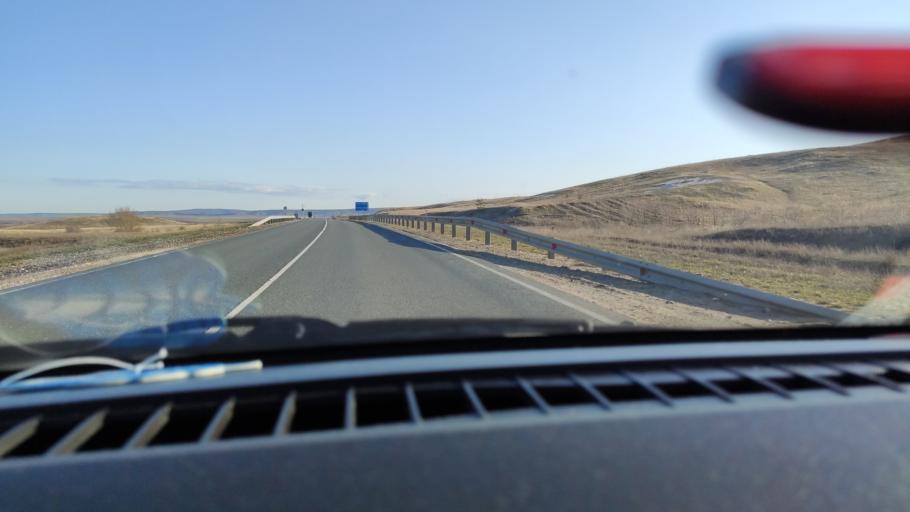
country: RU
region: Saratov
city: Alekseyevka
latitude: 52.3428
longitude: 47.9356
